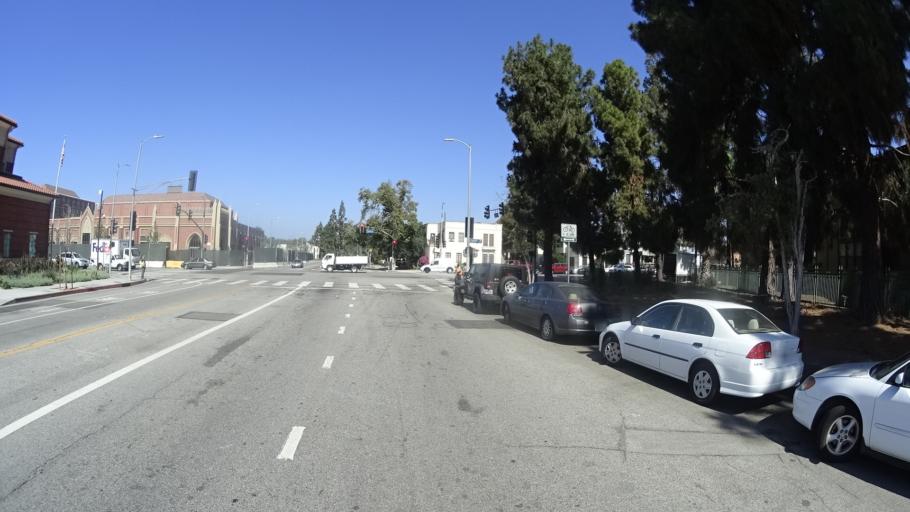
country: US
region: California
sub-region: Los Angeles County
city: Los Angeles
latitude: 34.0273
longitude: -118.2835
